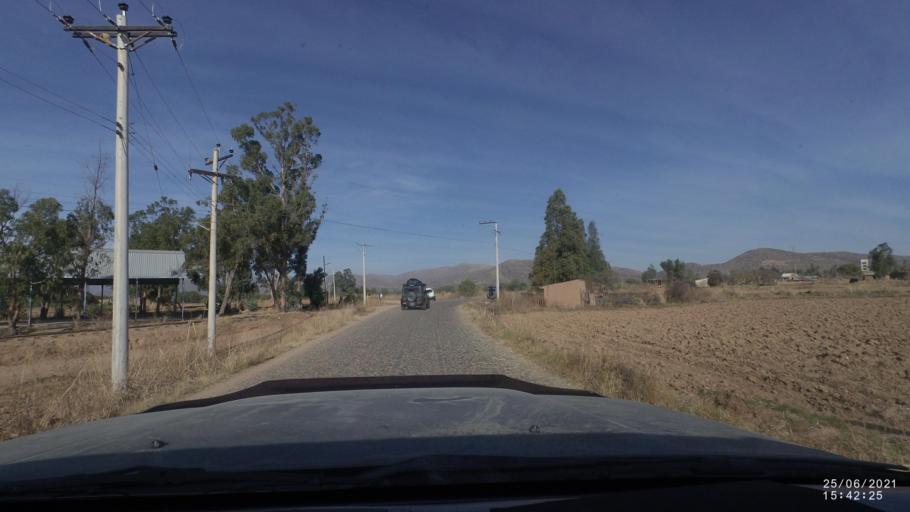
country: BO
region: Cochabamba
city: Cliza
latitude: -17.6392
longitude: -65.9121
